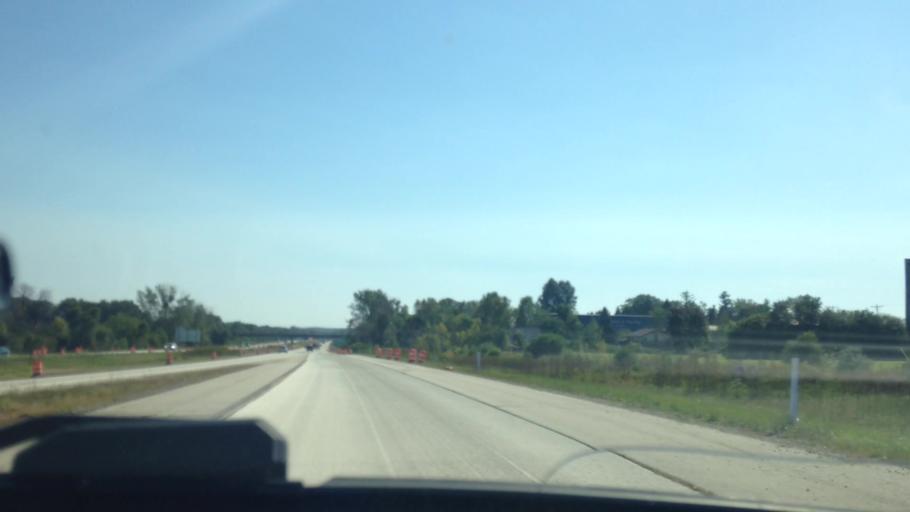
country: US
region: Wisconsin
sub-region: Ozaukee County
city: Grafton
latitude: 43.3359
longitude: -87.9248
